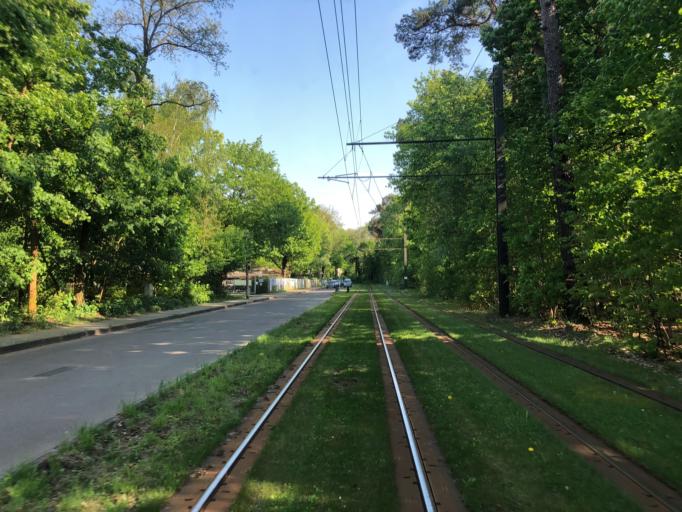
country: DE
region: Berlin
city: Schmockwitz
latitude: 52.3979
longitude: 13.6277
